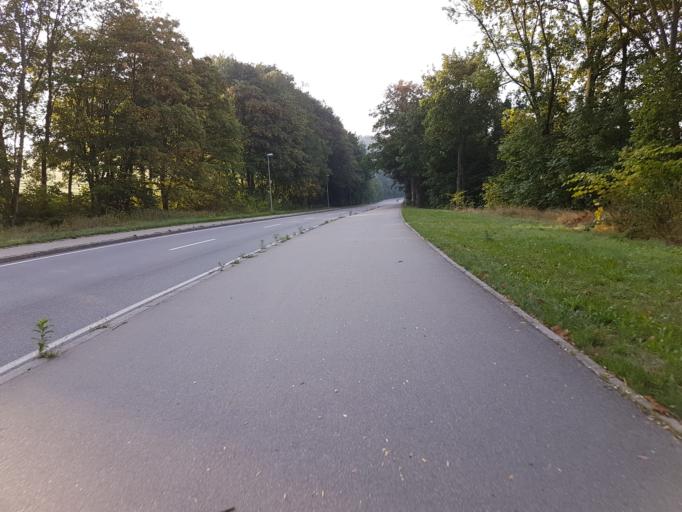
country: DE
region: Saxony
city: Taura
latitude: 50.9246
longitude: 12.8555
